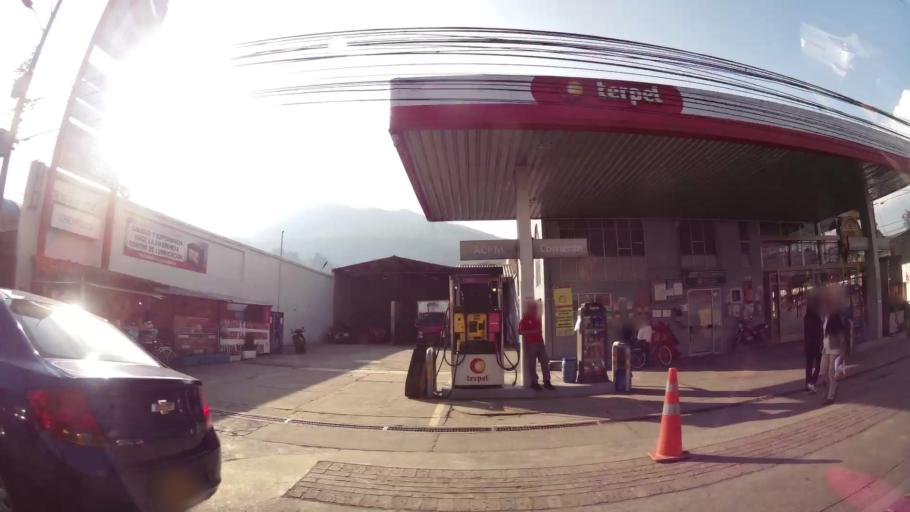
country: CO
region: Cundinamarca
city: Cota
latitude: 4.8090
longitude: -74.1026
